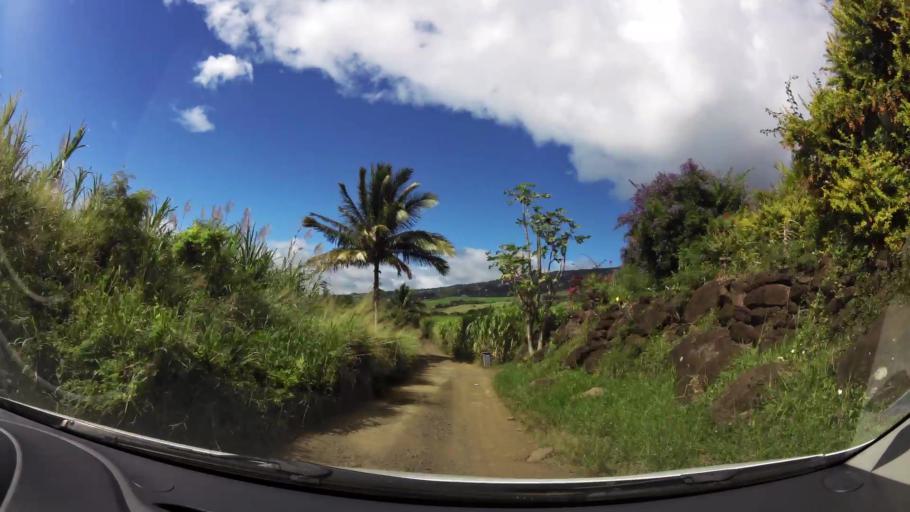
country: RE
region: Reunion
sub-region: Reunion
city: Sainte-Marie
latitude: -20.9295
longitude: 55.5014
